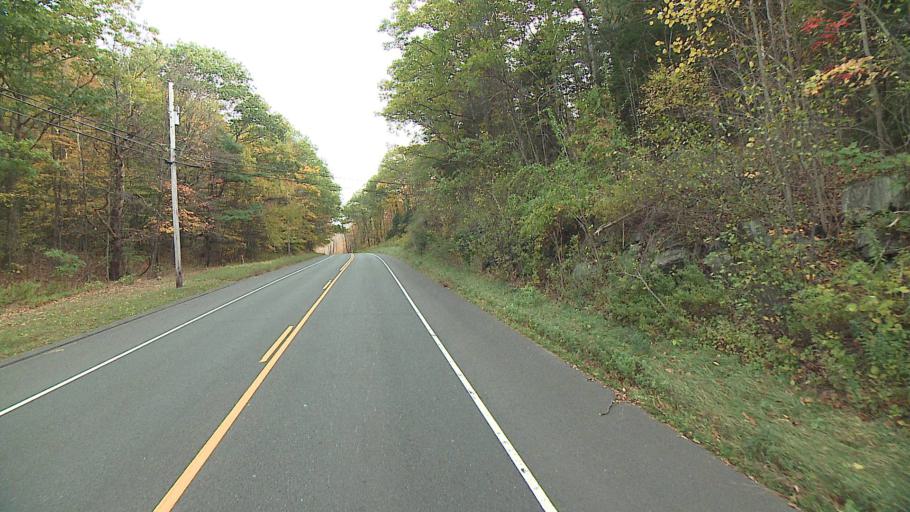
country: US
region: Connecticut
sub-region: Litchfield County
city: Winchester Center
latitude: 41.9835
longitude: -73.1658
